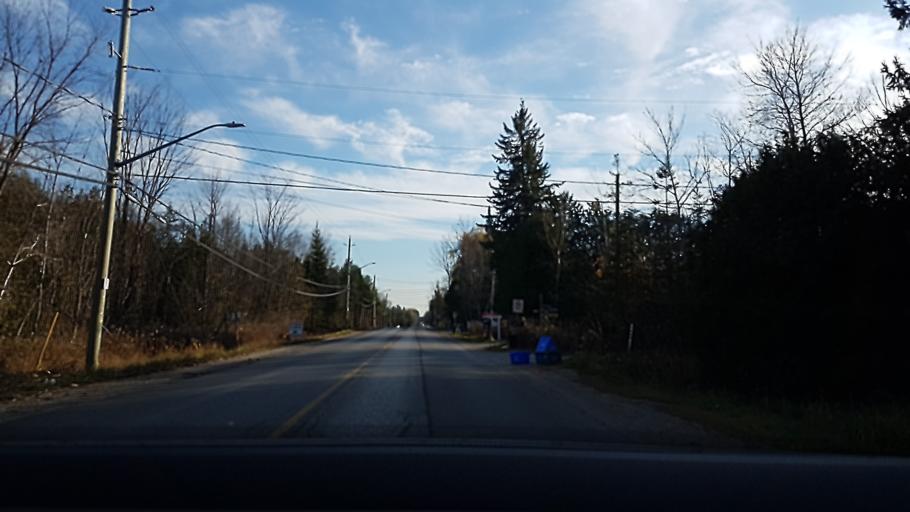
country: CA
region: Ontario
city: Innisfil
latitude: 44.3388
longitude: -79.5454
